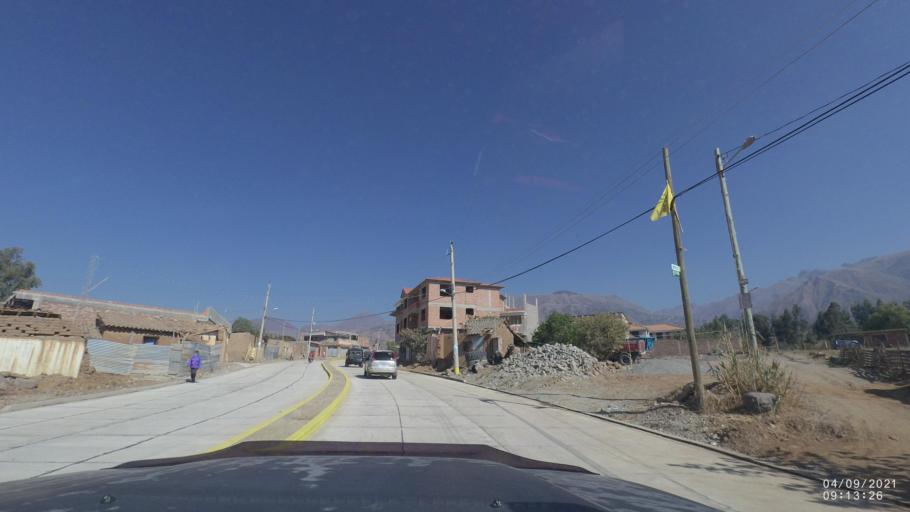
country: BO
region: Cochabamba
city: Sipe Sipe
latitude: -17.3824
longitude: -66.3427
